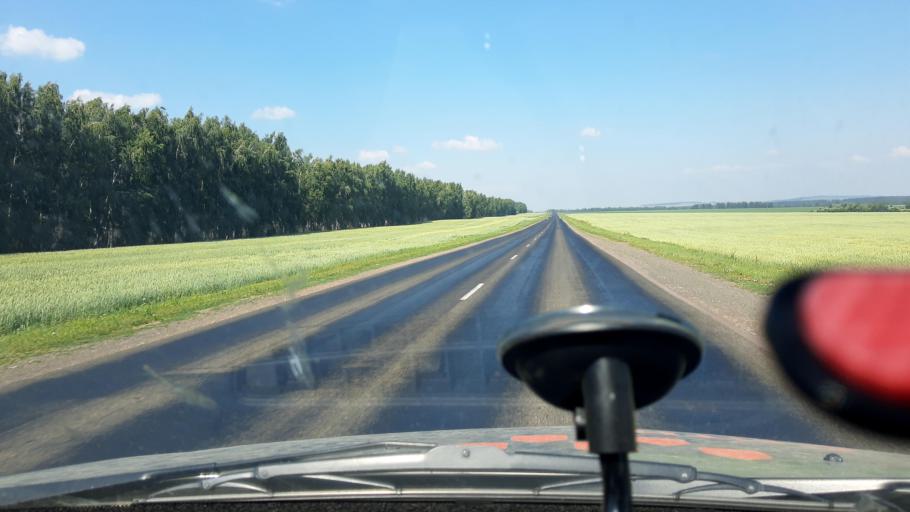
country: RU
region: Bashkortostan
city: Chekmagush
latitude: 55.0783
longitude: 54.6361
